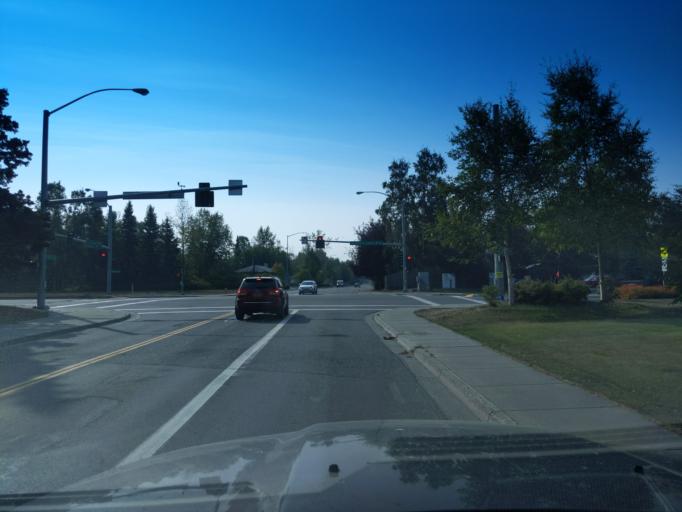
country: US
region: Alaska
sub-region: Anchorage Municipality
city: Anchorage
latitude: 61.1958
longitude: -149.9430
